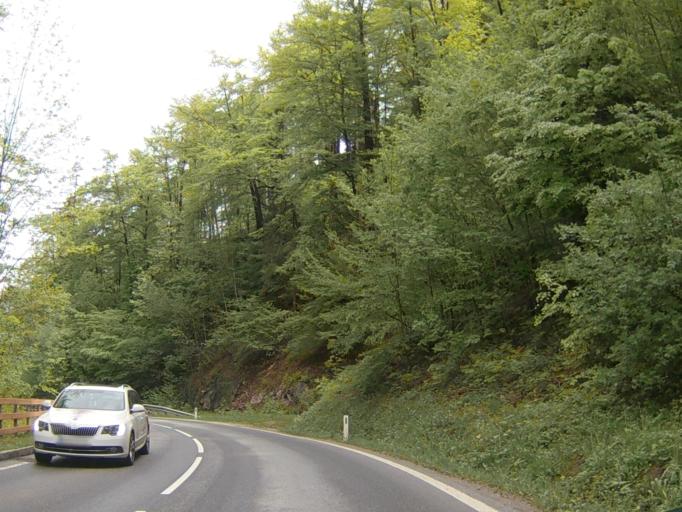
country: AT
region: Salzburg
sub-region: Politischer Bezirk Hallein
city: Hallein
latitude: 47.6769
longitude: 13.0862
